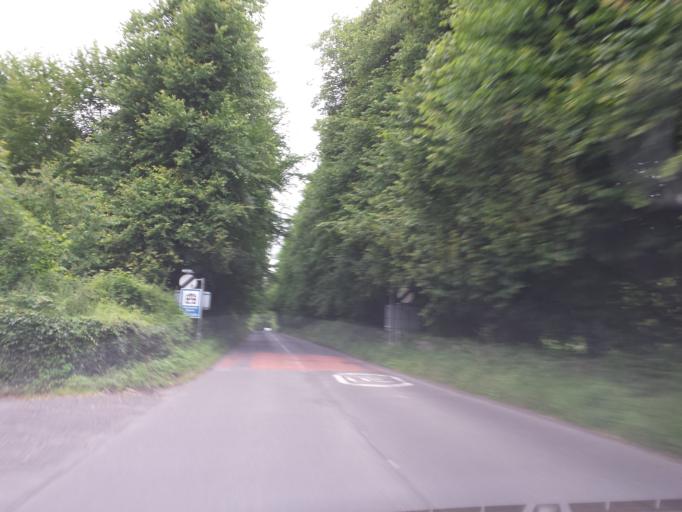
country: GB
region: Scotland
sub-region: Dumfries and Galloway
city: Dumfries
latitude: 54.9812
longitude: -3.6228
